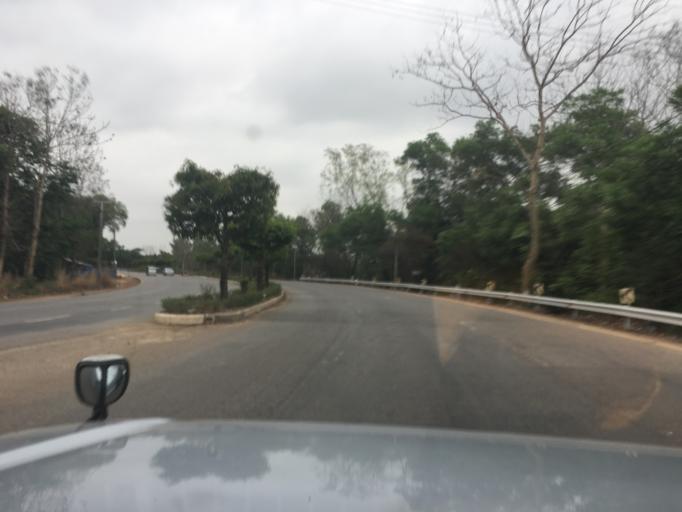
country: MM
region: Bago
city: Thanatpin
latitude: 17.2094
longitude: 96.4161
